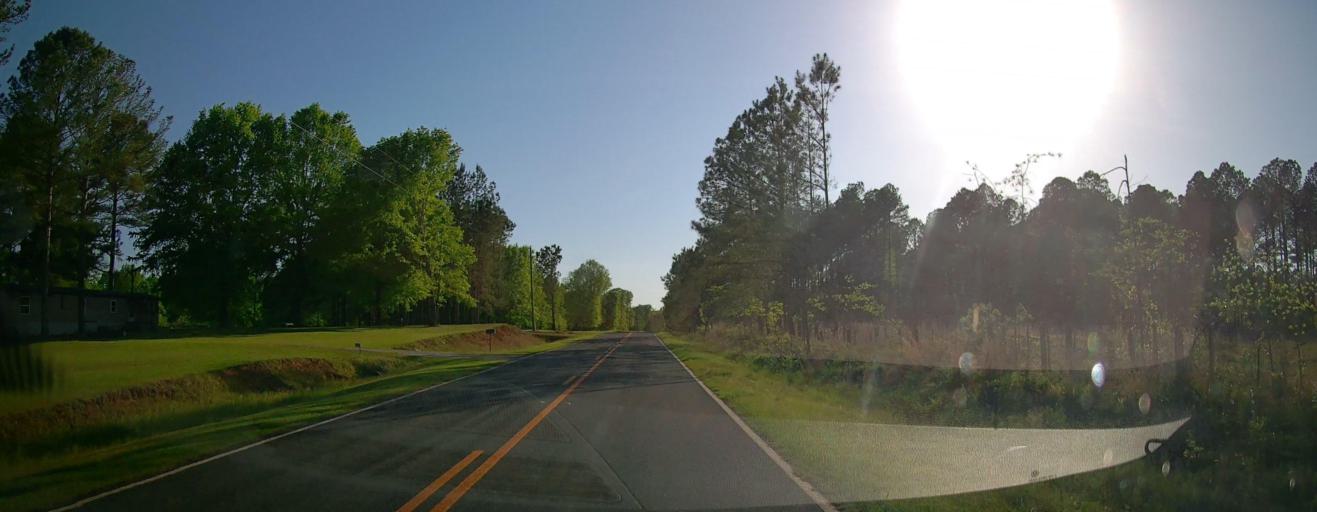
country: US
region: Georgia
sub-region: Macon County
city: Marshallville
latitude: 32.3884
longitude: -83.8510
